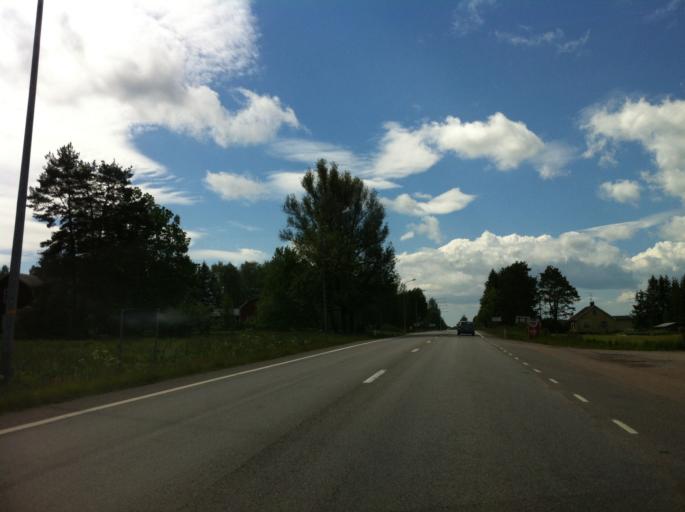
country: SE
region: Vaermland
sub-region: Saffle Kommun
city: Saeffle
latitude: 59.1893
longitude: 13.0187
